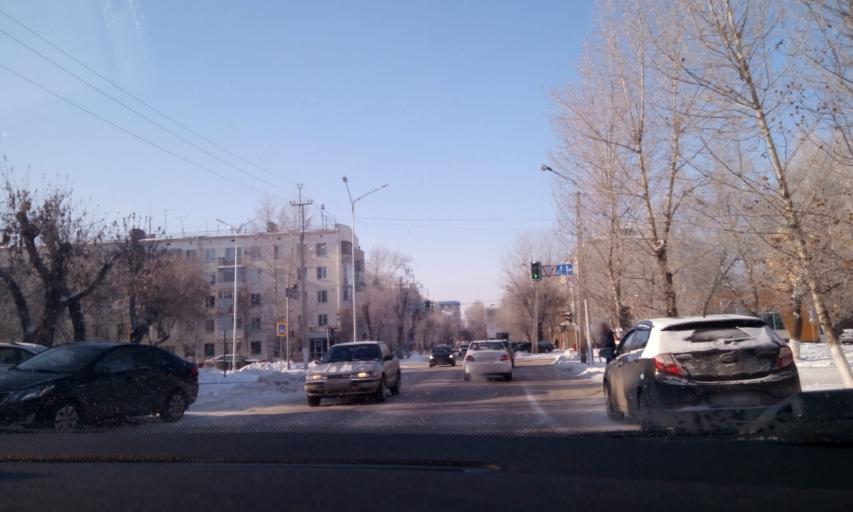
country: KZ
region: Astana Qalasy
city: Astana
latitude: 51.1792
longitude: 71.4219
